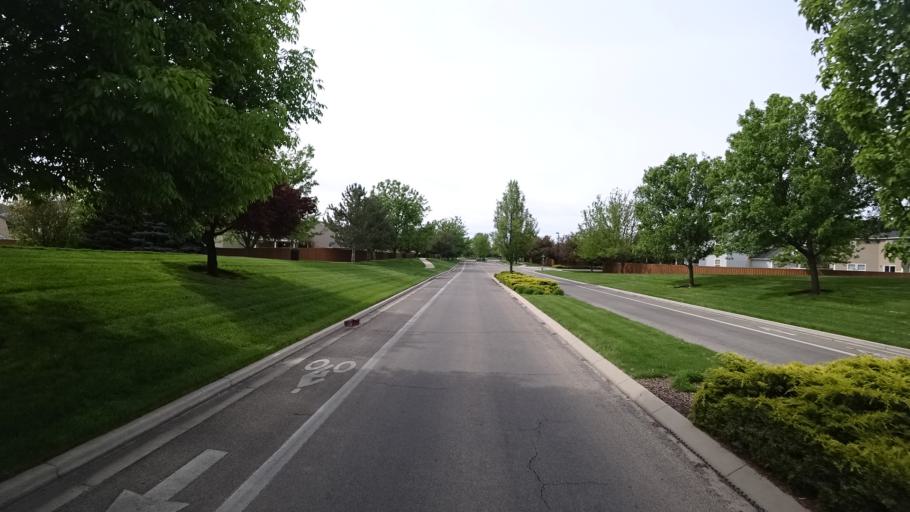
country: US
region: Idaho
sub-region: Ada County
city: Garden City
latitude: 43.5411
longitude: -116.2993
